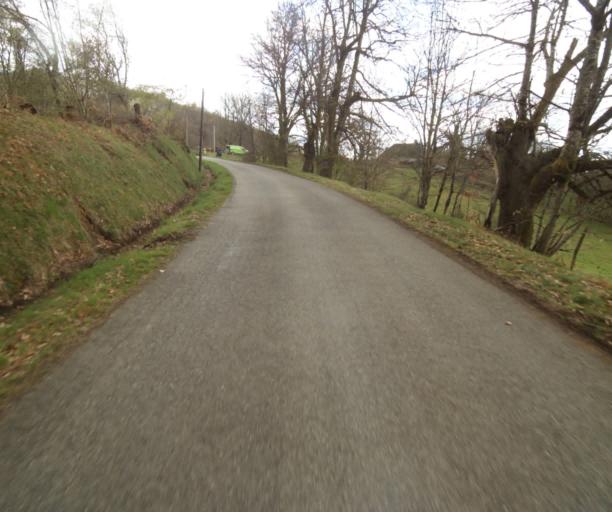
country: FR
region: Limousin
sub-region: Departement de la Correze
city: Laguenne
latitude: 45.2451
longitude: 1.8897
